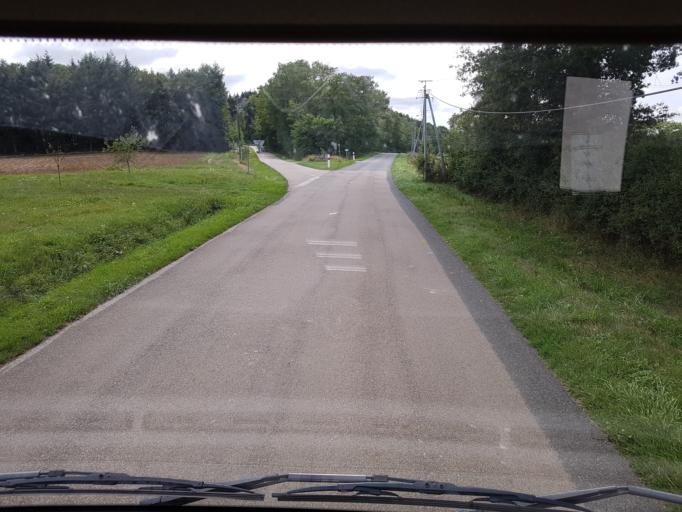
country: FR
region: Rhone-Alpes
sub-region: Departement de l'Ain
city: Villars-les-Dombes
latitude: 45.9581
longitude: 5.0943
